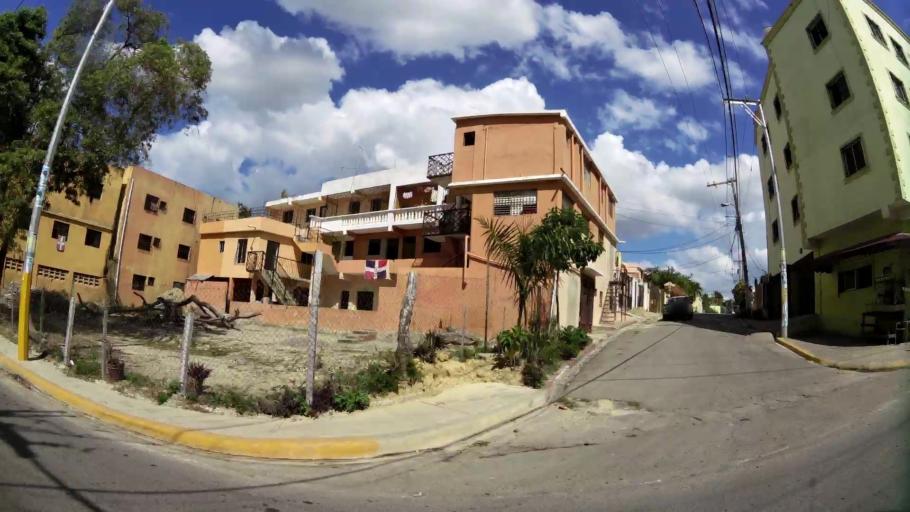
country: DO
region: Nacional
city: Ensanche Luperon
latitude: 18.5365
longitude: -69.8989
